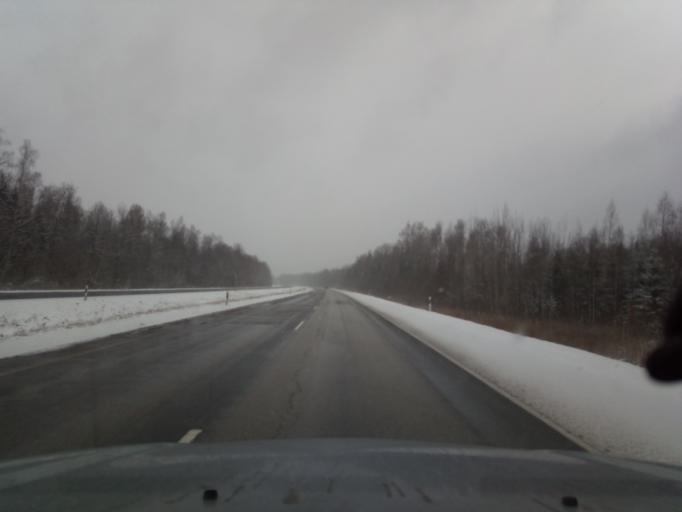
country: LT
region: Vilnius County
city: Ukmerge
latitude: 55.4355
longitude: 24.6746
